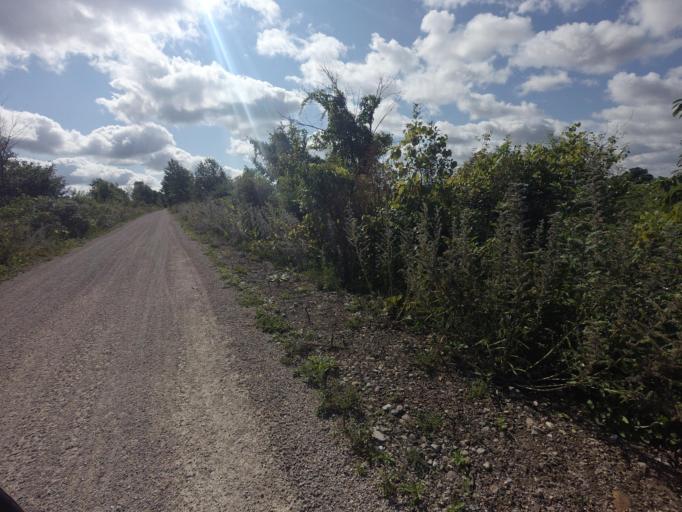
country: CA
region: Ontario
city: Huron East
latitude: 43.7218
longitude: -81.4007
